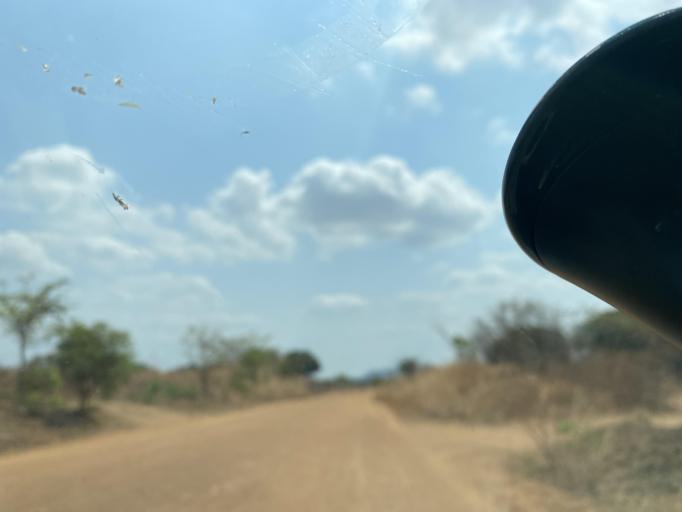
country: ZM
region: Lusaka
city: Chongwe
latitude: -15.5918
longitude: 28.7964
